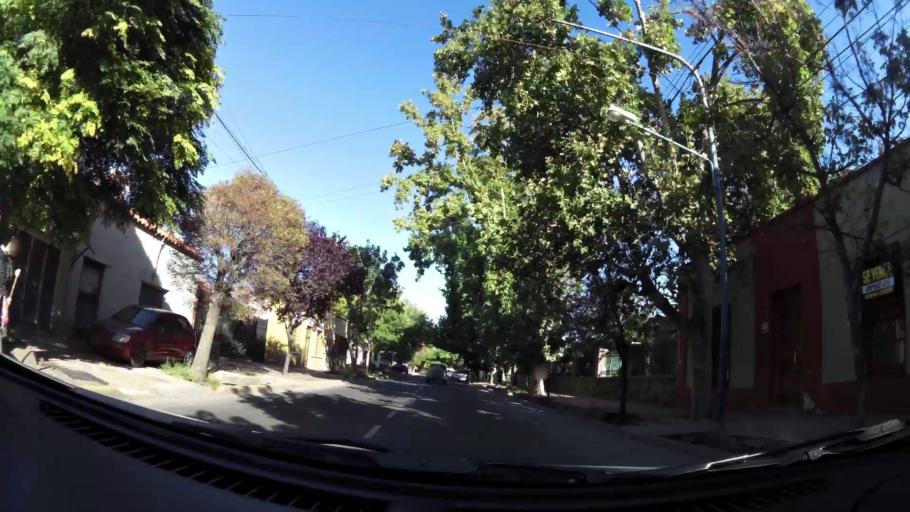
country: AR
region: Mendoza
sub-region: Departamento de Godoy Cruz
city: Godoy Cruz
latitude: -32.9300
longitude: -68.8421
